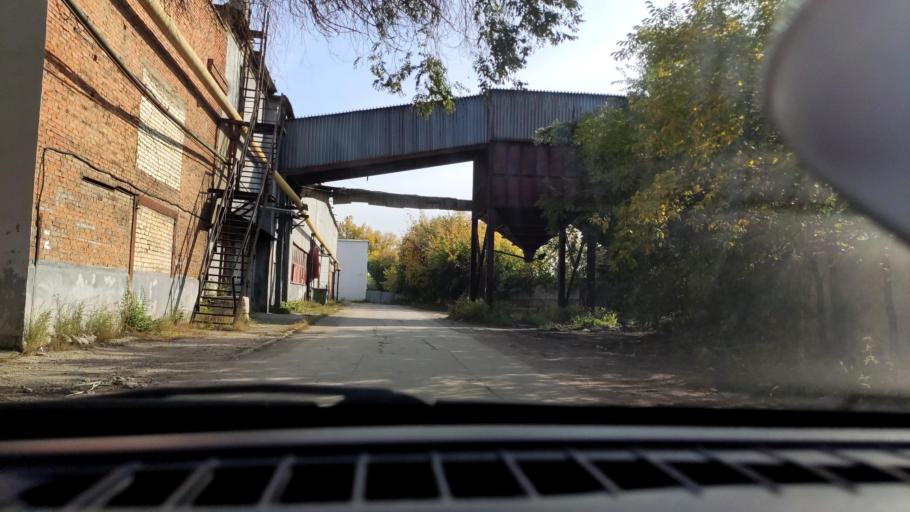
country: RU
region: Samara
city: Samara
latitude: 53.1903
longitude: 50.2591
